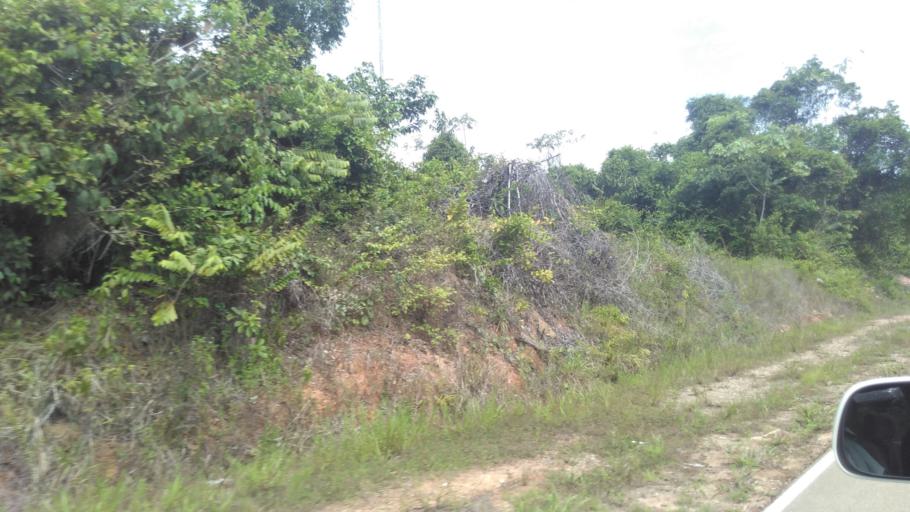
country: SR
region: Brokopondo
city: Brownsweg
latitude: 4.5566
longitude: -55.3668
